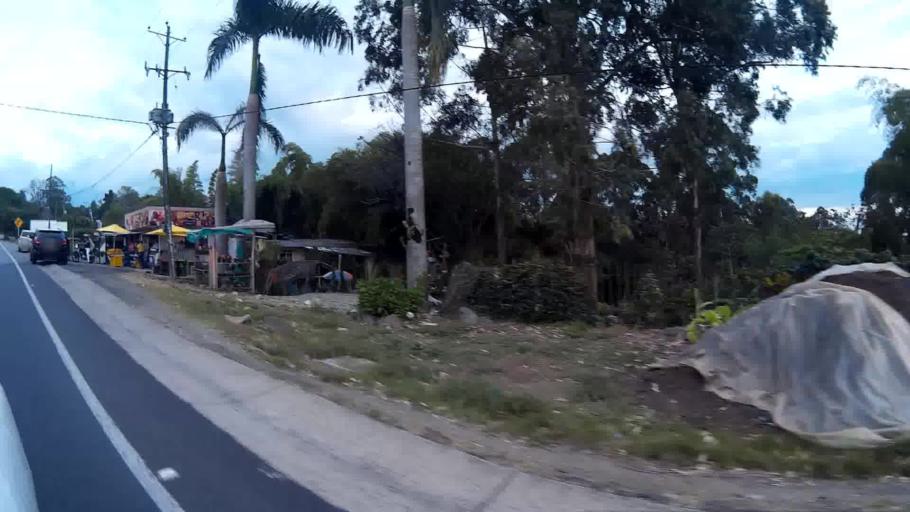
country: CO
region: Risaralda
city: Pereira
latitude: 4.7557
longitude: -75.6768
